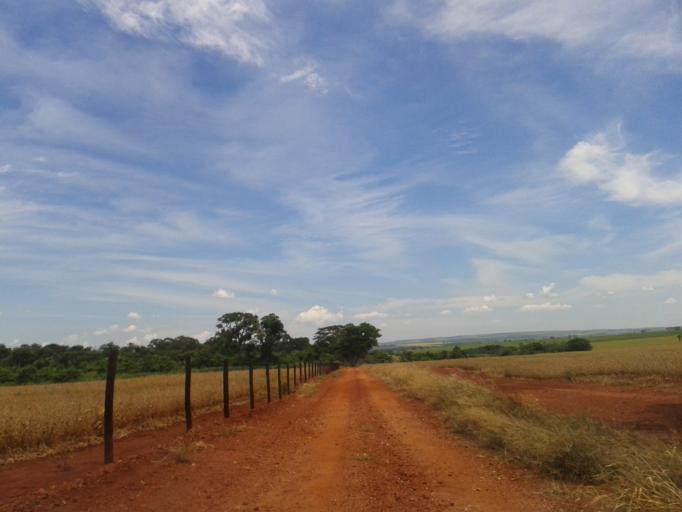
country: BR
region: Minas Gerais
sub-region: Capinopolis
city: Capinopolis
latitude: -18.6635
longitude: -49.7301
